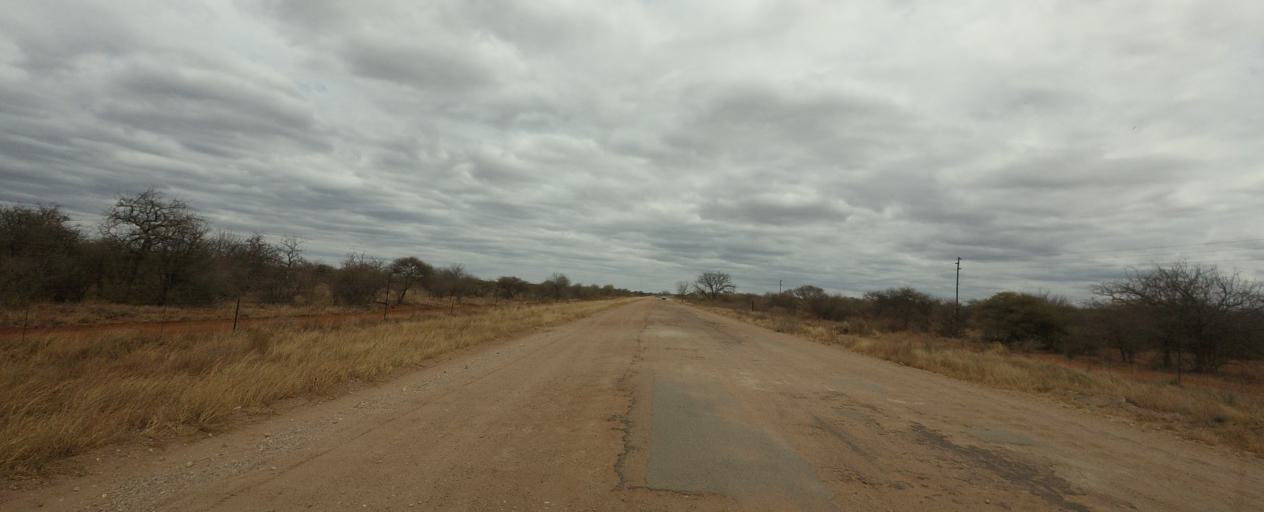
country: BW
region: Central
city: Mathathane
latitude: -22.7127
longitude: 28.5612
